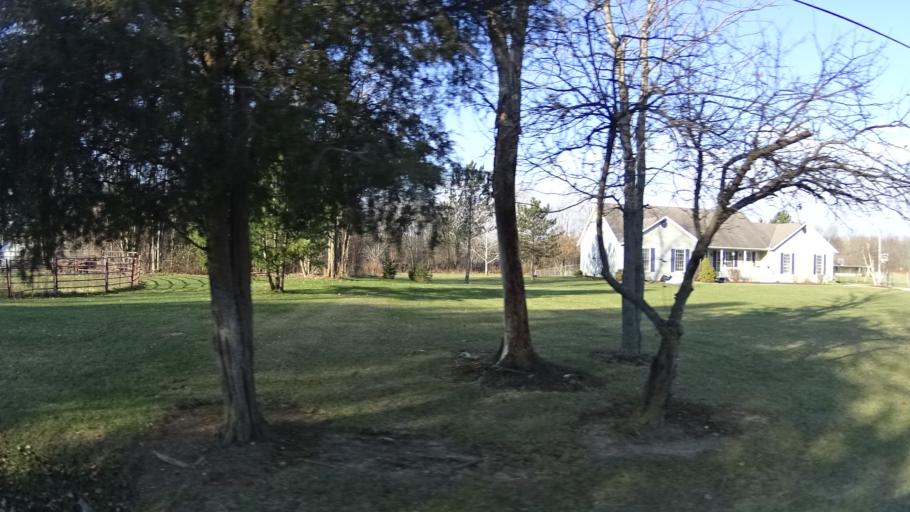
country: US
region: Ohio
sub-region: Lorain County
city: Lagrange
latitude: 41.2675
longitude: -82.1575
